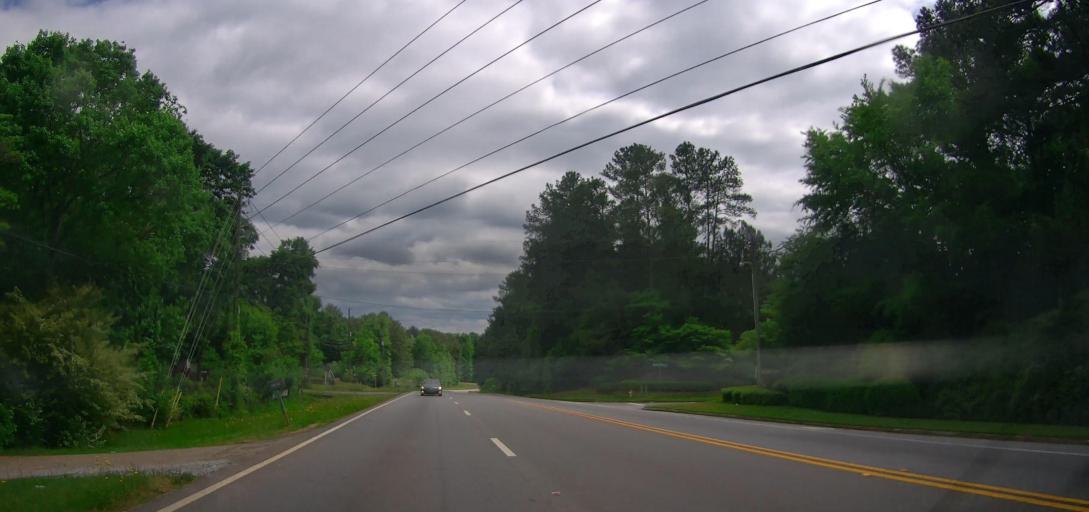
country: US
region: Georgia
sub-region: DeKalb County
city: Pine Mountain
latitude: 33.6086
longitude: -84.0953
